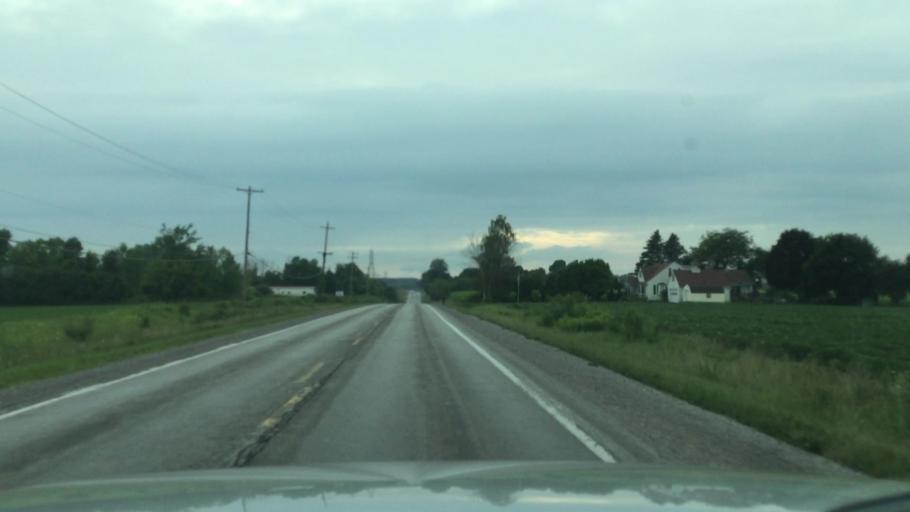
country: US
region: Michigan
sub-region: Saginaw County
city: Bridgeport
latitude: 43.3358
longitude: -83.8243
